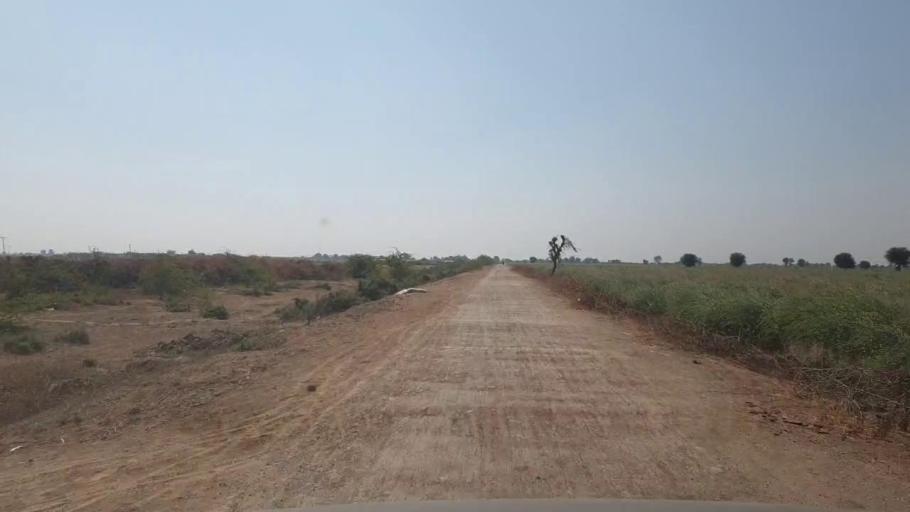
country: PK
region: Sindh
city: Digri
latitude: 25.2332
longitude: 69.2225
